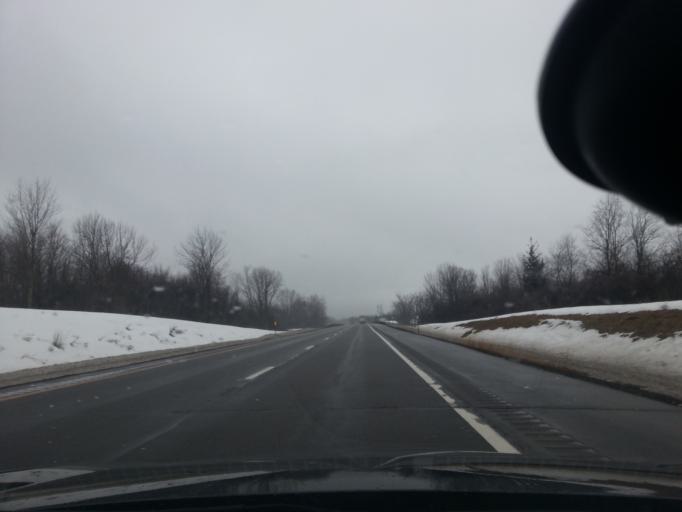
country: US
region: New York
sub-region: Oswego County
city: Pulaski
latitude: 43.5959
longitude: -76.1020
